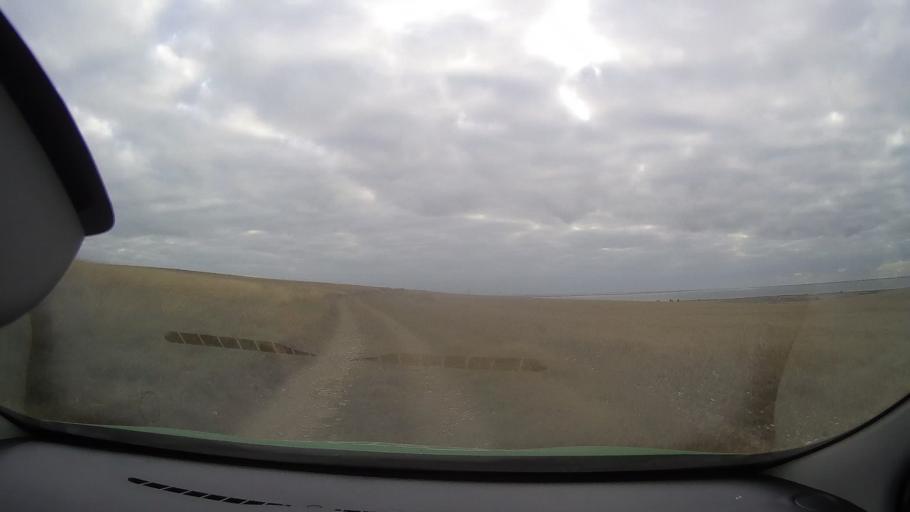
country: RO
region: Tulcea
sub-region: Comuna Jurilovca
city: Jurilovca
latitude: 44.7648
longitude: 28.9254
